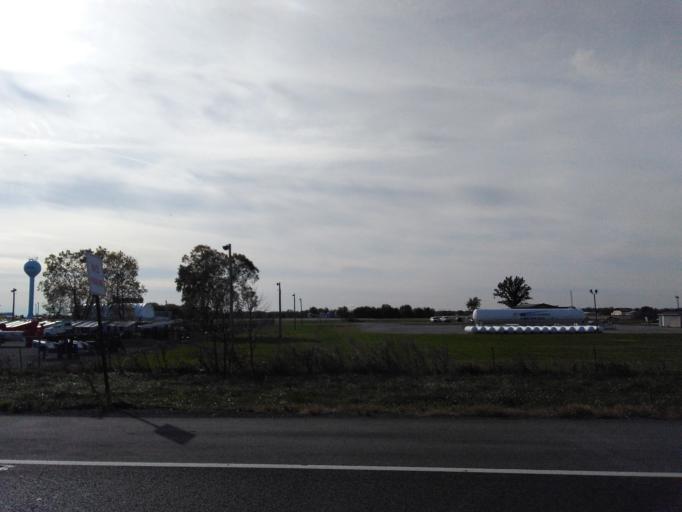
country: US
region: Illinois
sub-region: Madison County
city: Highland
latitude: 38.7861
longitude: -89.6360
